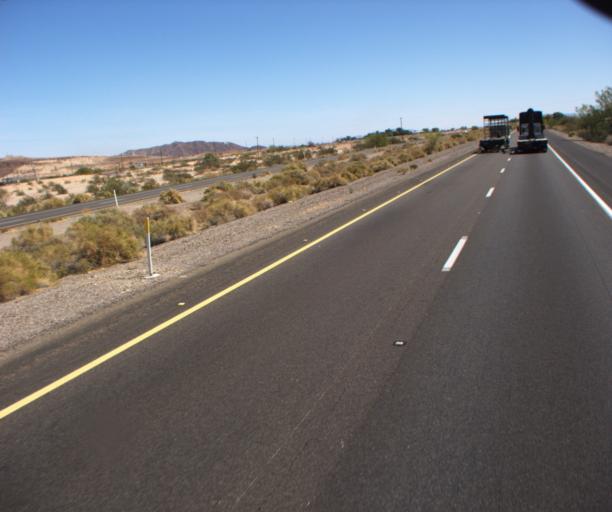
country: US
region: Arizona
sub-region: Yuma County
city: Wellton
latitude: 32.6753
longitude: -114.0600
